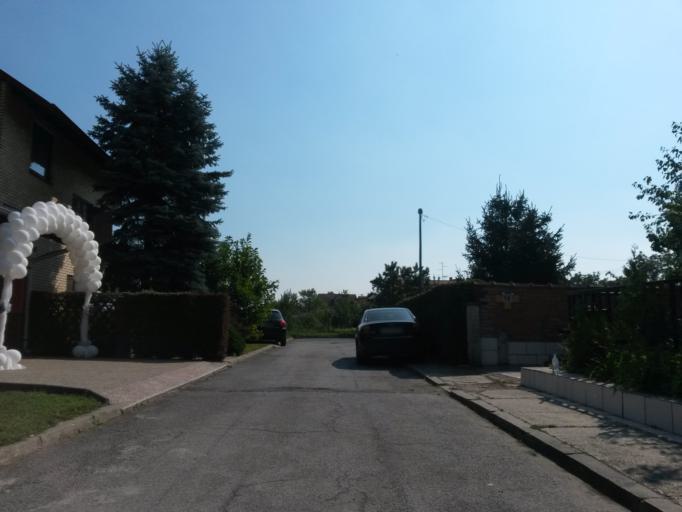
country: HR
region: Osjecko-Baranjska
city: Brijest
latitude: 45.5427
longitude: 18.6631
